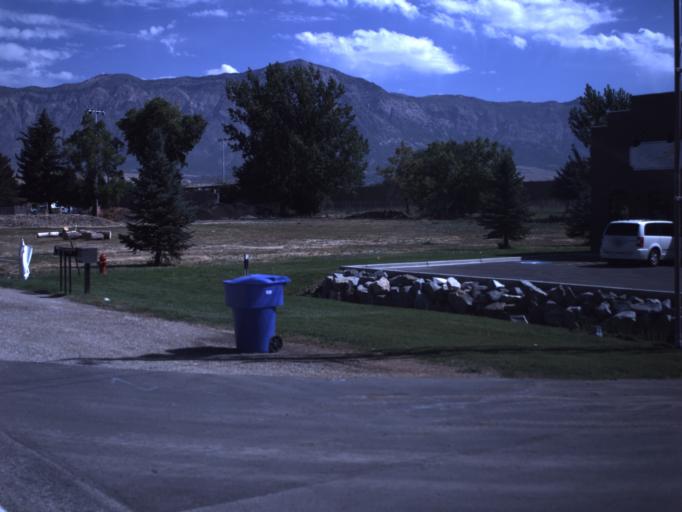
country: US
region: Utah
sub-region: Weber County
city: Farr West
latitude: 41.2942
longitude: -112.0278
